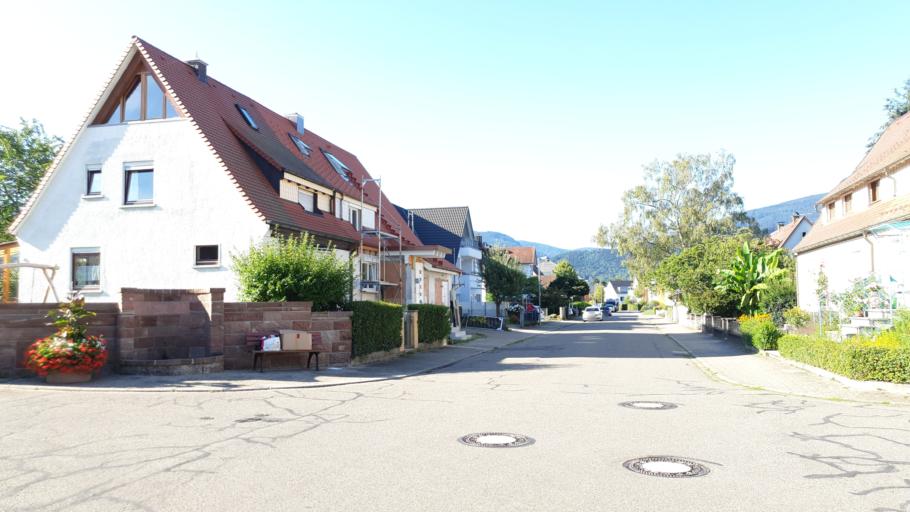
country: DE
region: Baden-Wuerttemberg
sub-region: Freiburg Region
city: Kirchzarten
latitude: 47.9644
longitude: 7.9585
